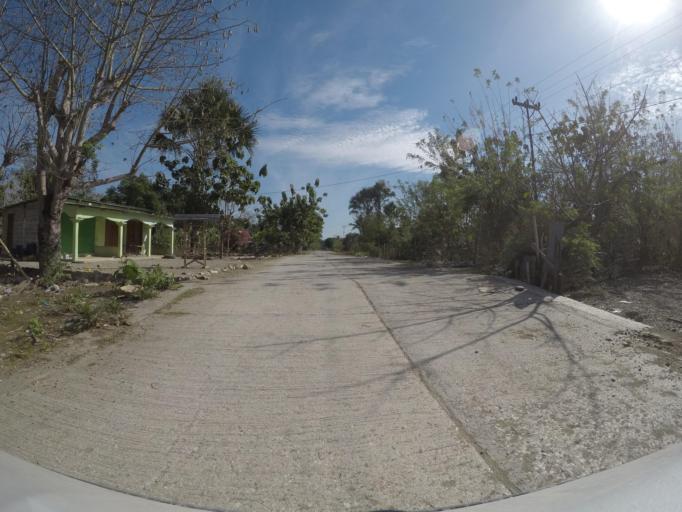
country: TL
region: Bobonaro
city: Maliana
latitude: -8.8564
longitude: 125.2179
